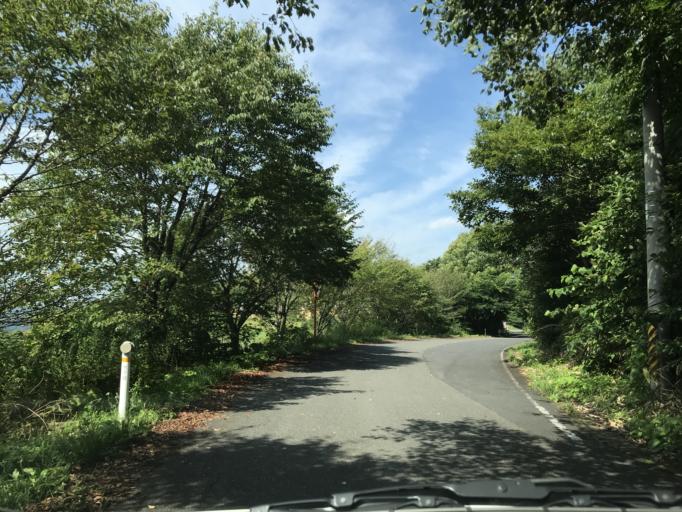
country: JP
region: Iwate
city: Ofunato
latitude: 38.9861
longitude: 141.4561
